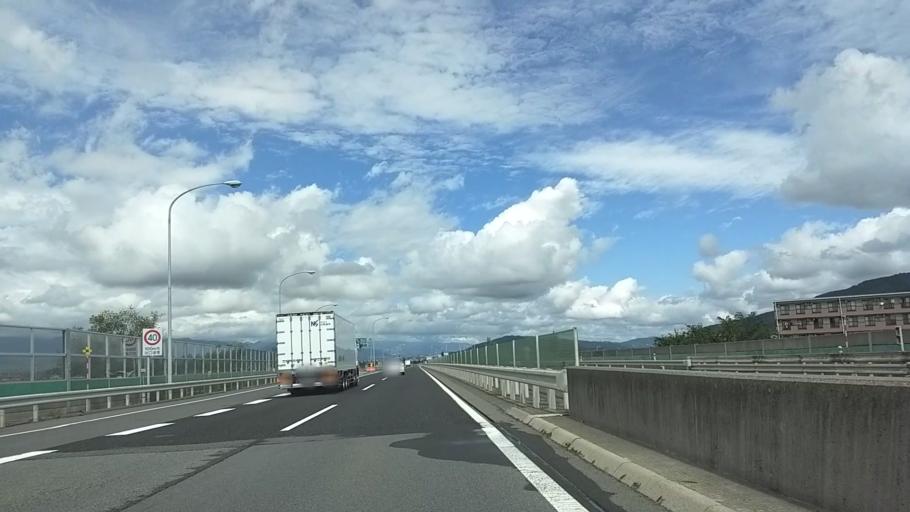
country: JP
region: Nagano
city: Toyoshina
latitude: 36.2952
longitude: 137.9268
